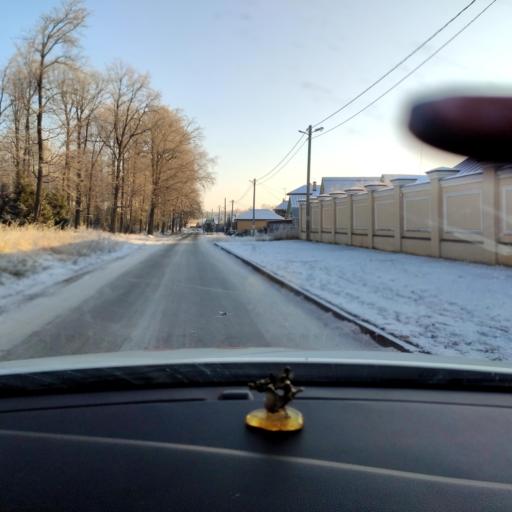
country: RU
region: Tatarstan
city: Stolbishchi
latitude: 55.6732
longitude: 49.1063
